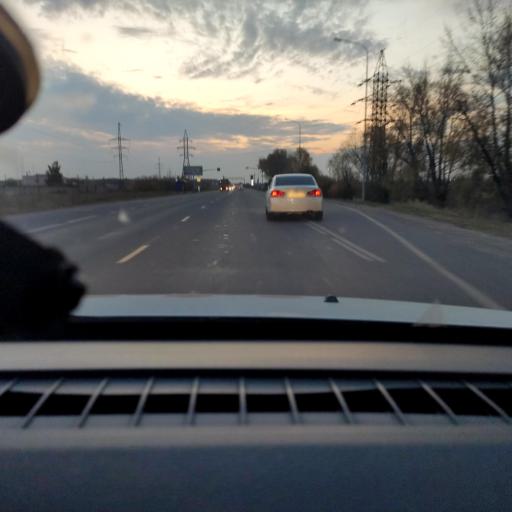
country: RU
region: Samara
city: Samara
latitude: 53.1304
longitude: 50.1493
